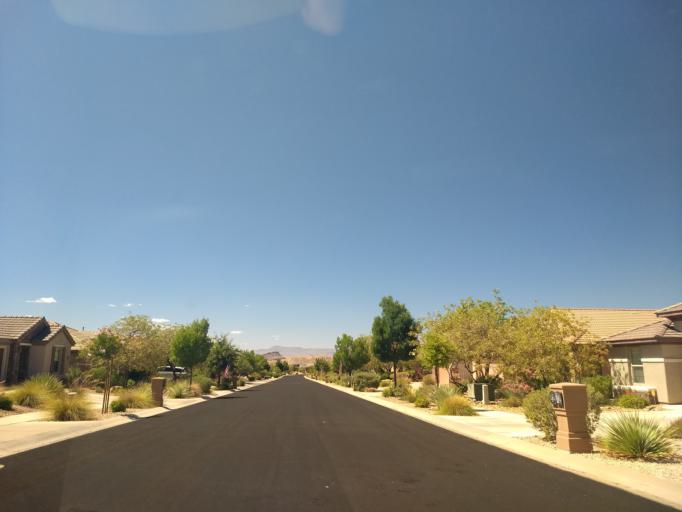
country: US
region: Utah
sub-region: Washington County
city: Washington
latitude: 37.1473
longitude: -113.4661
